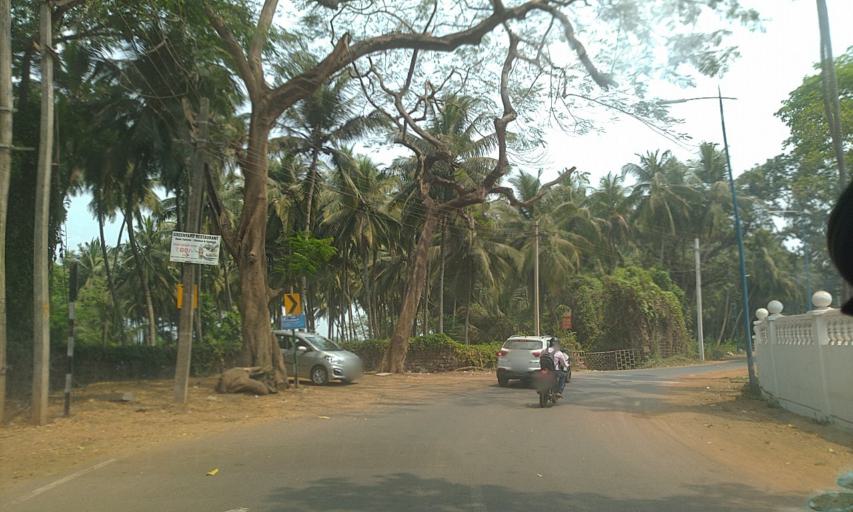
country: IN
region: Goa
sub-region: North Goa
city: Jua
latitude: 15.5035
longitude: 73.9100
